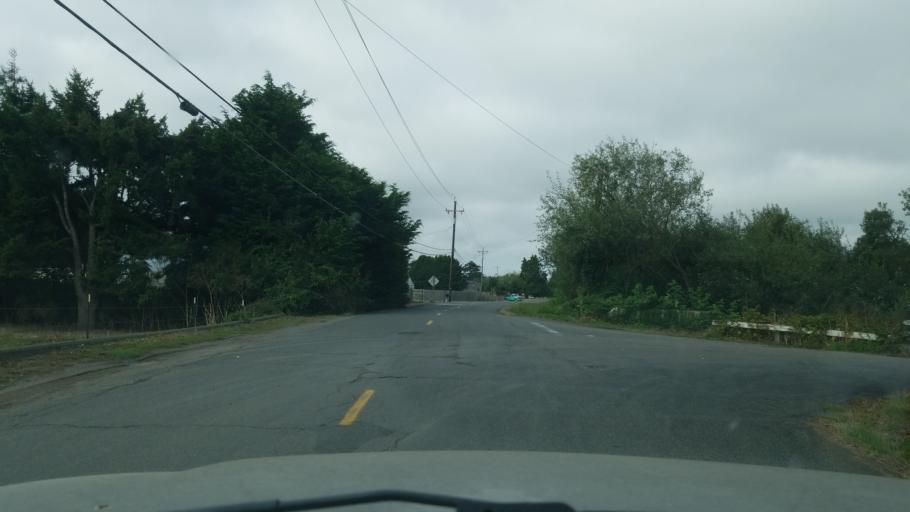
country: US
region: California
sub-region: Humboldt County
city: Ferndale
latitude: 40.5946
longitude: -124.2500
